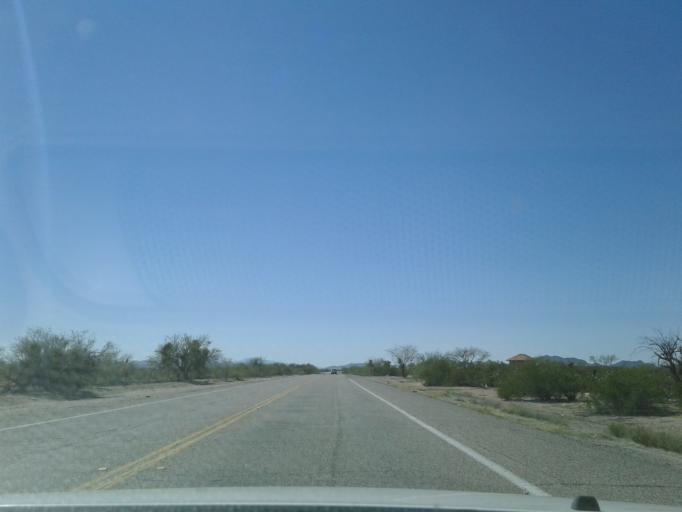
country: US
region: Arizona
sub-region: Pima County
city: Avra Valley
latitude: 32.3857
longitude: -111.3099
